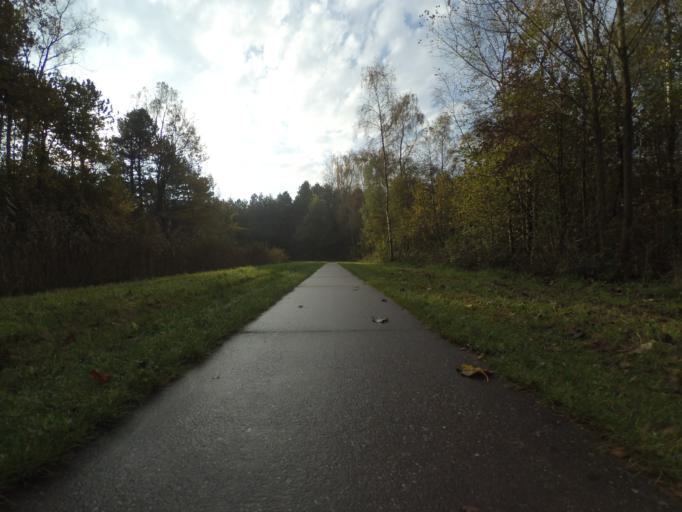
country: NL
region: Flevoland
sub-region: Gemeente Zeewolde
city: Zeewolde
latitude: 52.3059
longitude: 5.5351
